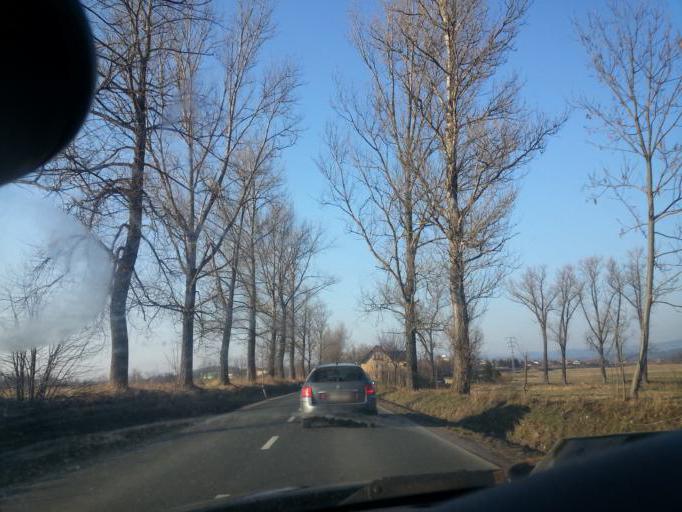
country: PL
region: Lower Silesian Voivodeship
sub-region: Powiat jeleniogorski
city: Myslakowice
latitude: 50.8413
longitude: 15.7869
